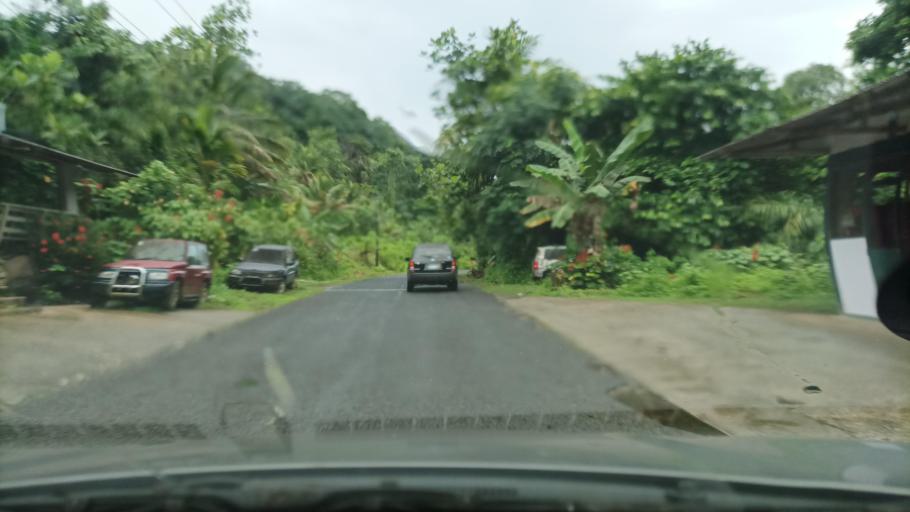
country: FM
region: Pohnpei
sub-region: Sokehs Municipality
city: Palikir - National Government Center
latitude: 6.8425
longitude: 158.1565
